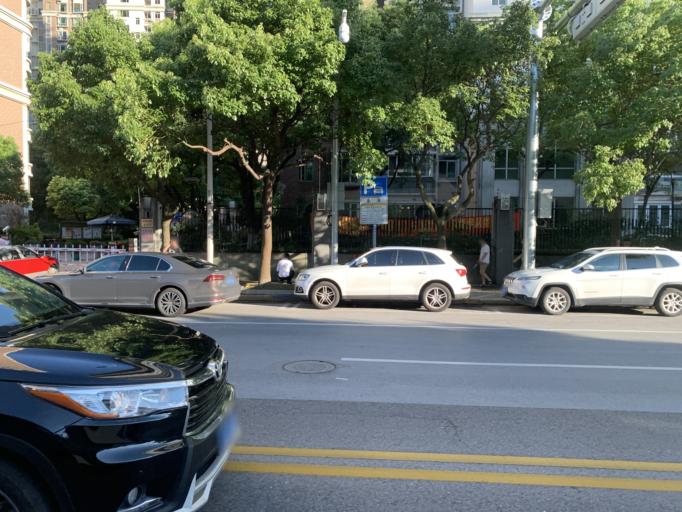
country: CN
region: Shanghai Shi
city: Huamu
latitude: 31.2268
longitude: 121.5530
